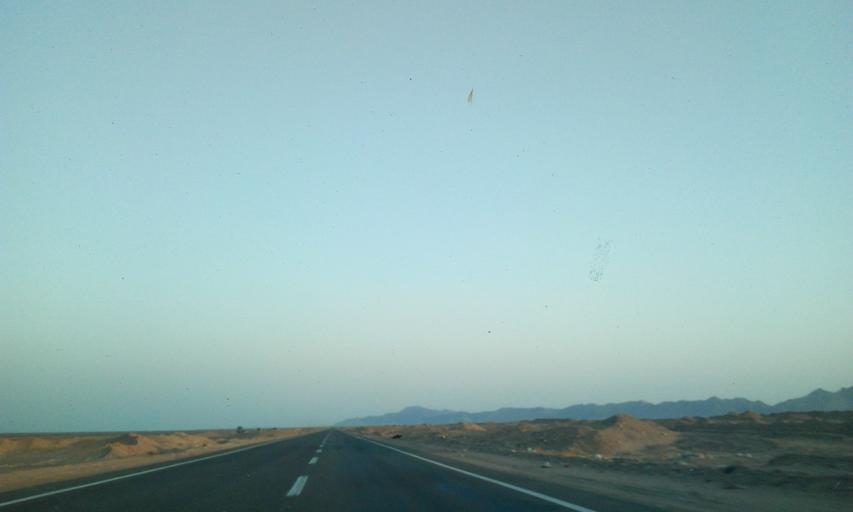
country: EG
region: Red Sea
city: El Gouna
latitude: 27.6206
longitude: 33.4994
